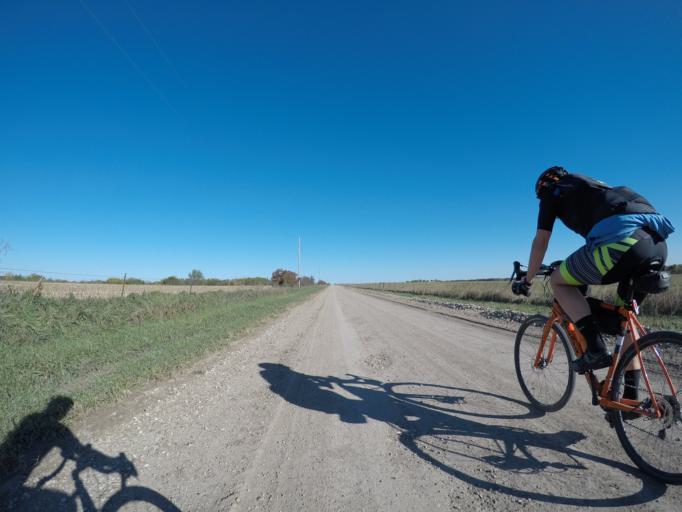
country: US
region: Kansas
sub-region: Morris County
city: Council Grove
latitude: 38.8306
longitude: -96.4085
